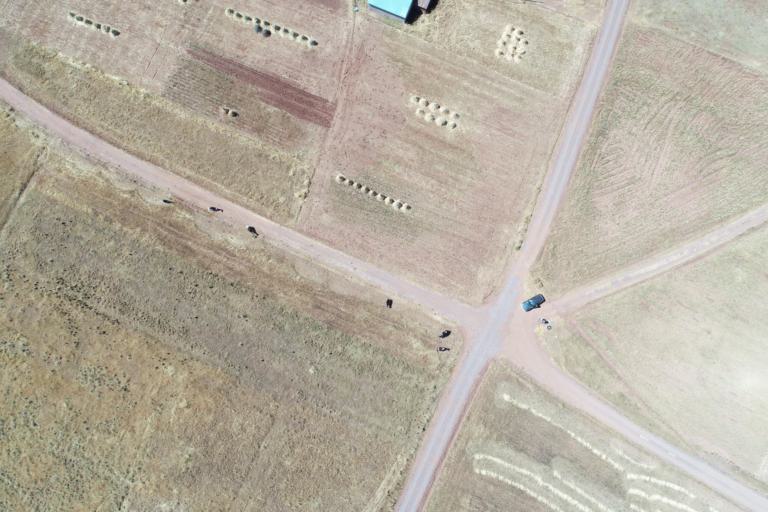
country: BO
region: La Paz
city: Tiahuanaco
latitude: -16.5941
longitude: -68.7722
